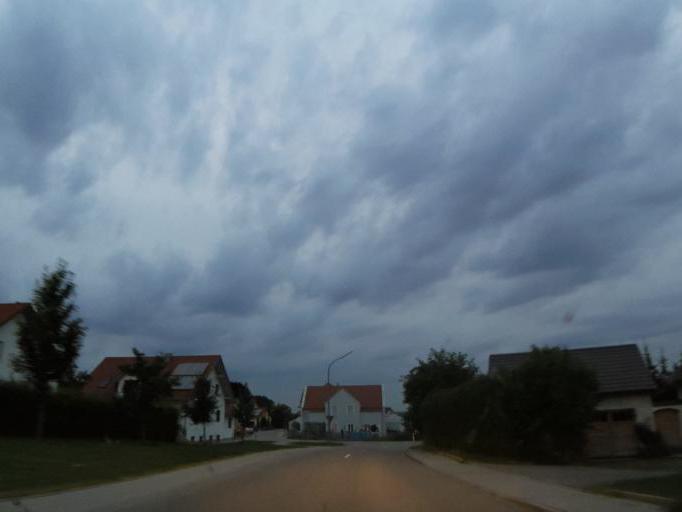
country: DE
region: Bavaria
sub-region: Upper Bavaria
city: Buch am Buchrain
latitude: 48.2181
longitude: 11.9906
